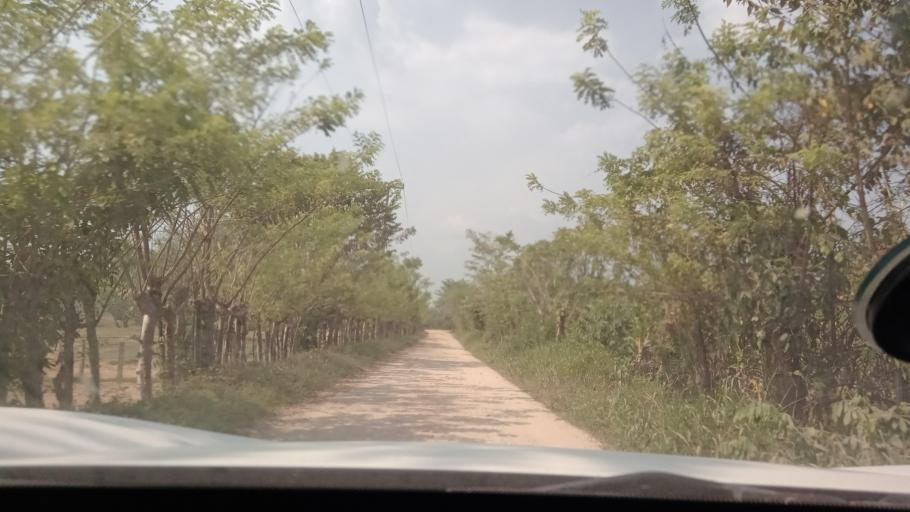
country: MX
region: Tabasco
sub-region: Huimanguillo
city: Francisco Rueda
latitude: 17.6813
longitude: -93.8622
